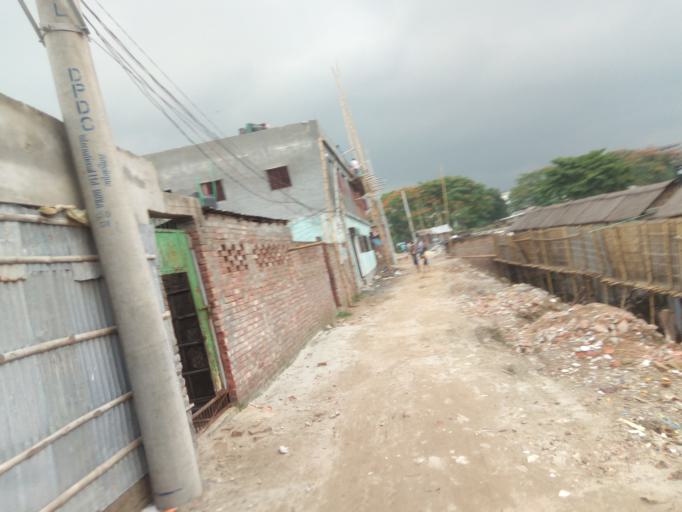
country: BD
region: Dhaka
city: Azimpur
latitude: 23.7376
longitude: 90.3591
